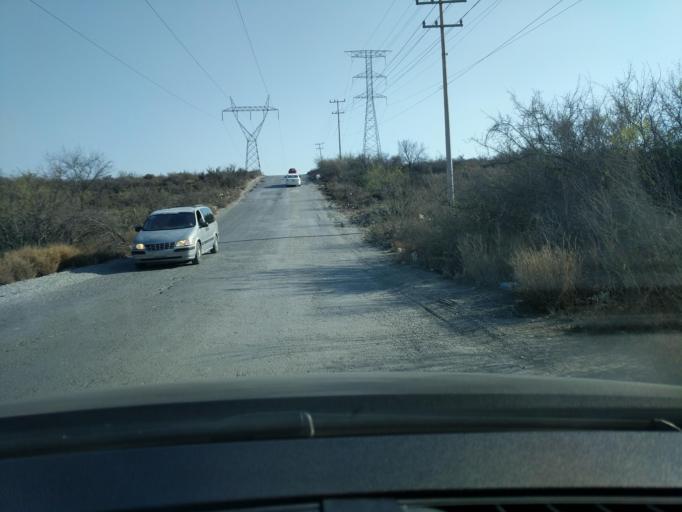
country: MX
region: Coahuila
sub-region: Ramos Arizpe
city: Ramos Arizpe
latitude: 25.5372
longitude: -100.9781
